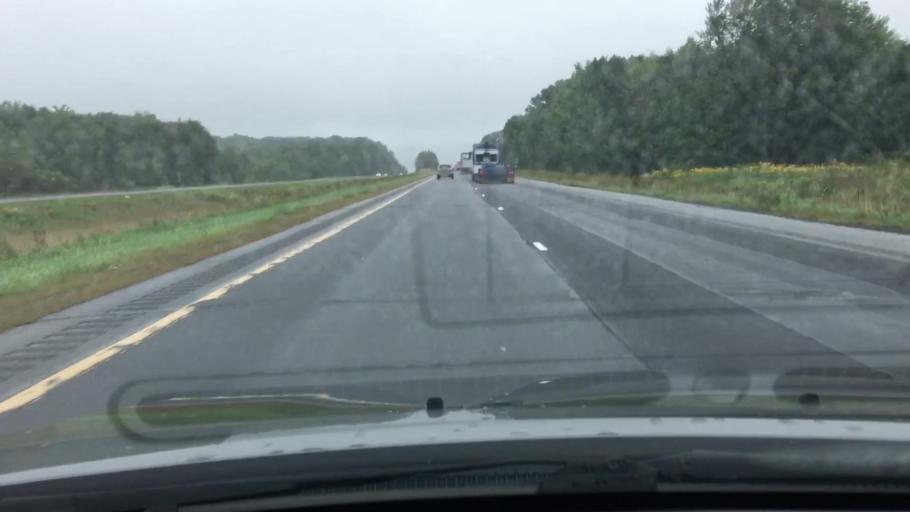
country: US
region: Pennsylvania
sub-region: Lackawanna County
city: Mount Cobb
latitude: 41.3750
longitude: -75.4516
